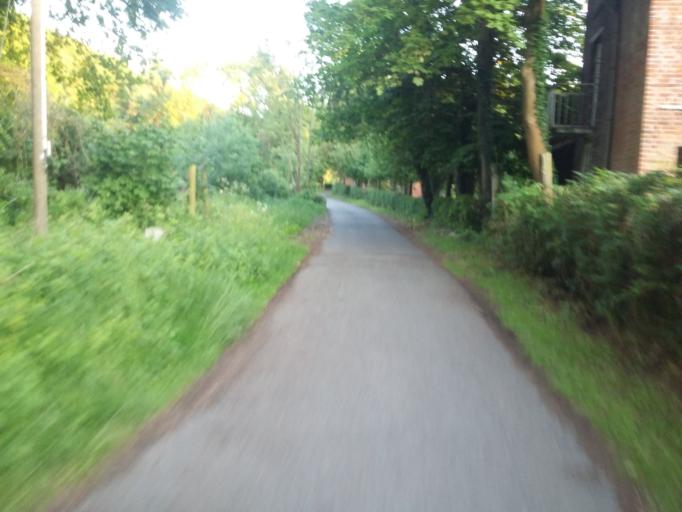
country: DE
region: North Rhine-Westphalia
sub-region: Regierungsbezirk Detmold
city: Vlotho
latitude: 52.1949
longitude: 8.8646
